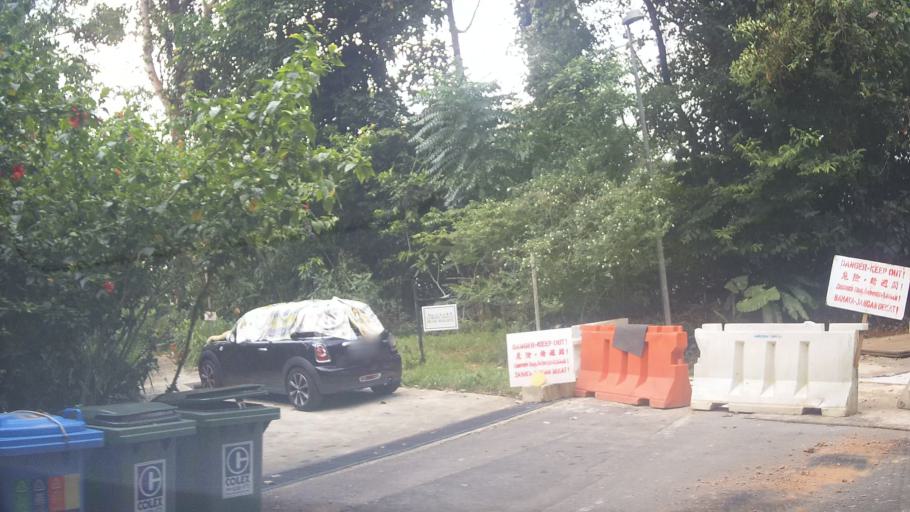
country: SG
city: Singapore
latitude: 1.3548
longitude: 103.7662
